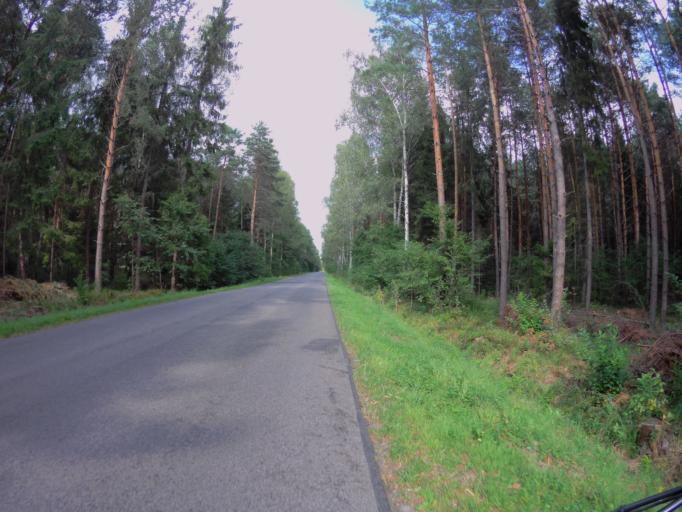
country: PL
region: Subcarpathian Voivodeship
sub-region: Powiat lezajski
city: Brzoza Krolewska
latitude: 50.2553
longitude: 22.3662
